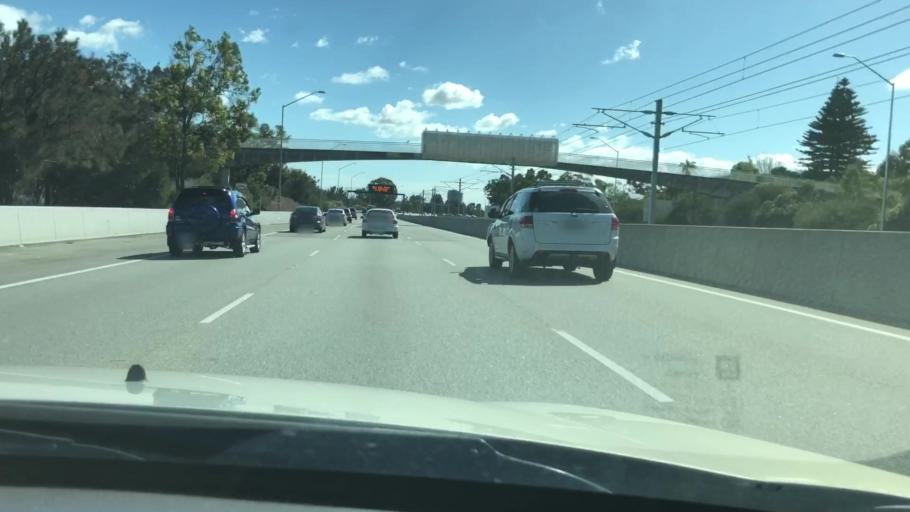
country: AU
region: Western Australia
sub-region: South Perth
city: Manning
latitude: -32.0247
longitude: 115.8596
